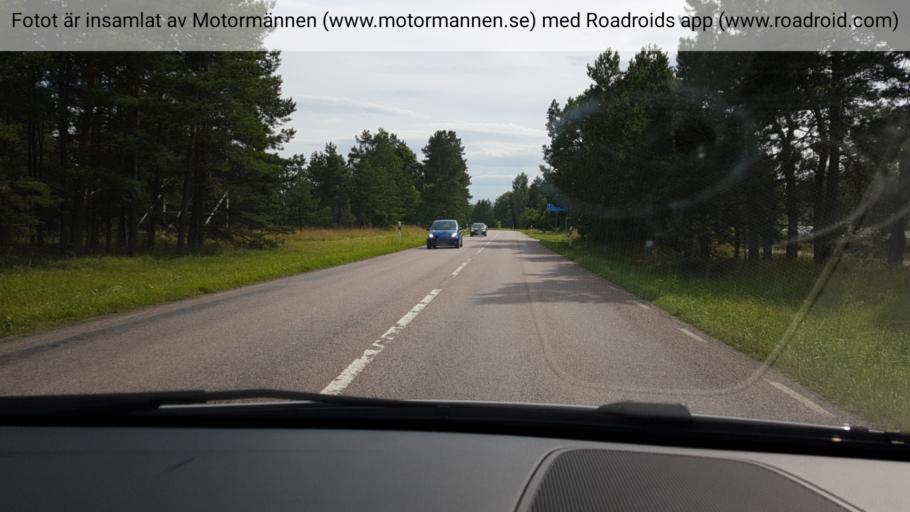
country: SE
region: Uppsala
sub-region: Osthammars Kommun
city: OEsthammar
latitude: 60.2473
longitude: 18.3476
